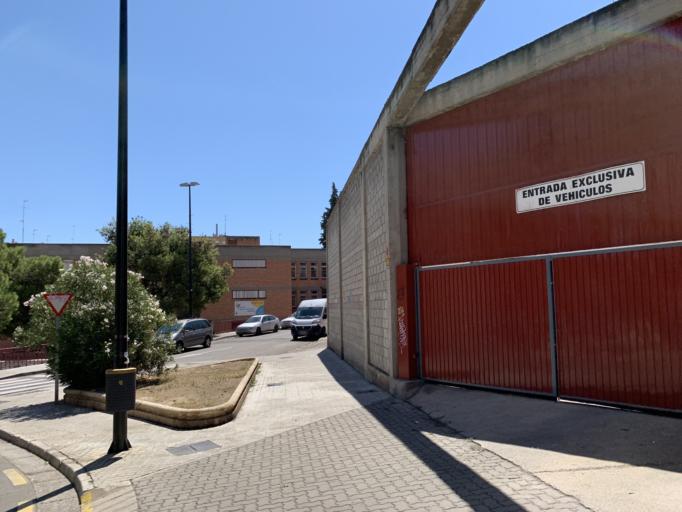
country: ES
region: Aragon
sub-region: Provincia de Zaragoza
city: Zaragoza
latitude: 41.6368
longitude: -0.8814
